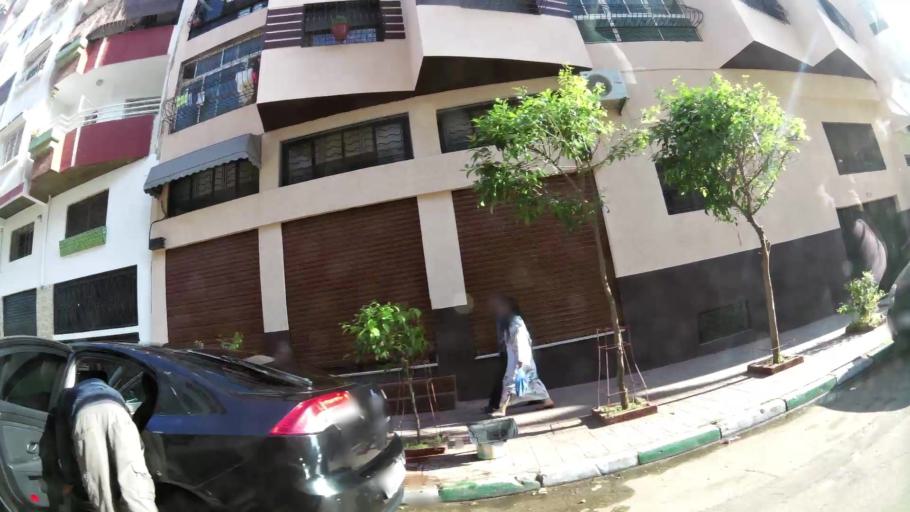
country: MA
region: Rabat-Sale-Zemmour-Zaer
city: Sale
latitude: 34.0468
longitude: -6.8039
